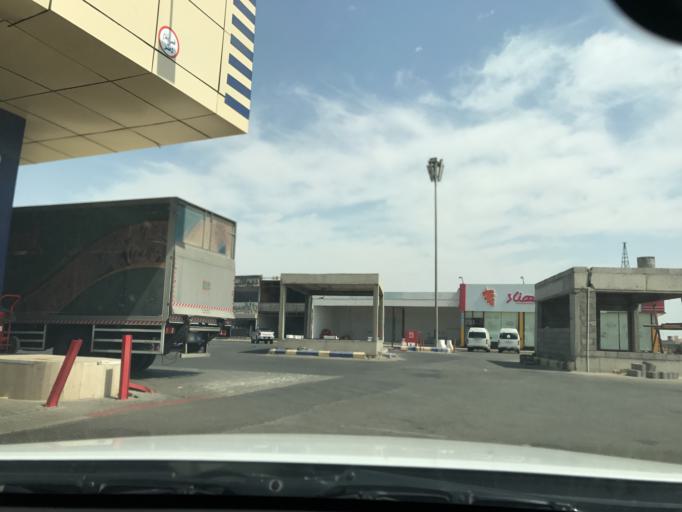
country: SA
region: Makkah
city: Jeddah
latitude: 21.3987
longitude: 39.4373
